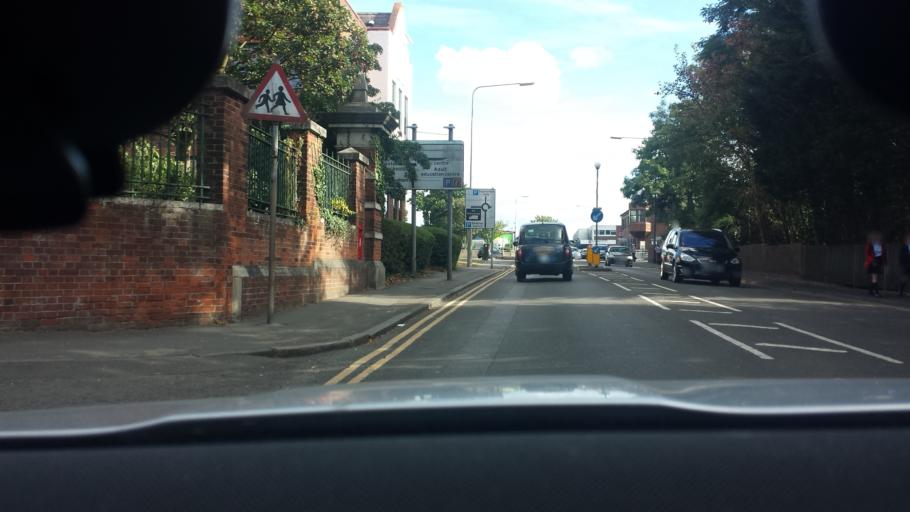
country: GB
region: England
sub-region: Kent
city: Swanley
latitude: 51.3982
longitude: 0.1716
